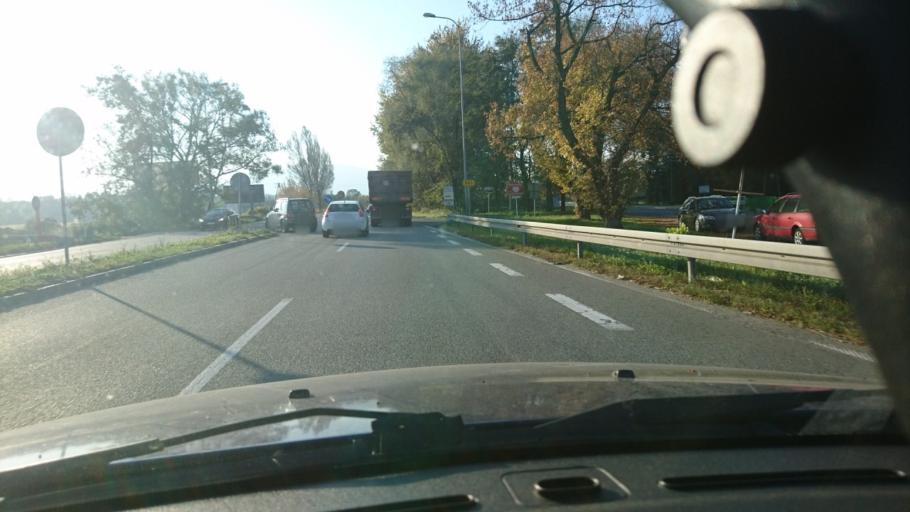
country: PL
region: Silesian Voivodeship
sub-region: Powiat cieszynski
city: Gorki Wielkie
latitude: 49.7818
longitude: 18.8065
